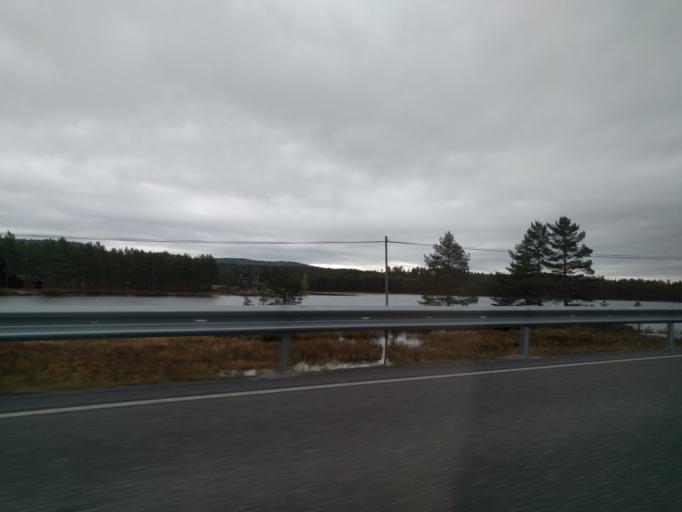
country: NO
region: Aust-Agder
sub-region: Evje og Hornnes
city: Evje
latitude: 58.5204
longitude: 7.7764
